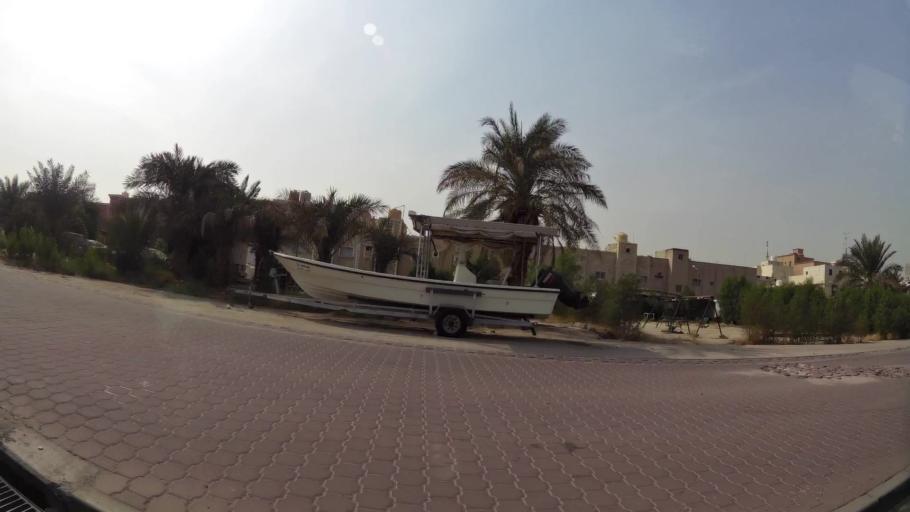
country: KW
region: Al Asimah
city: Ar Rabiyah
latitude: 29.2932
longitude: 47.9391
